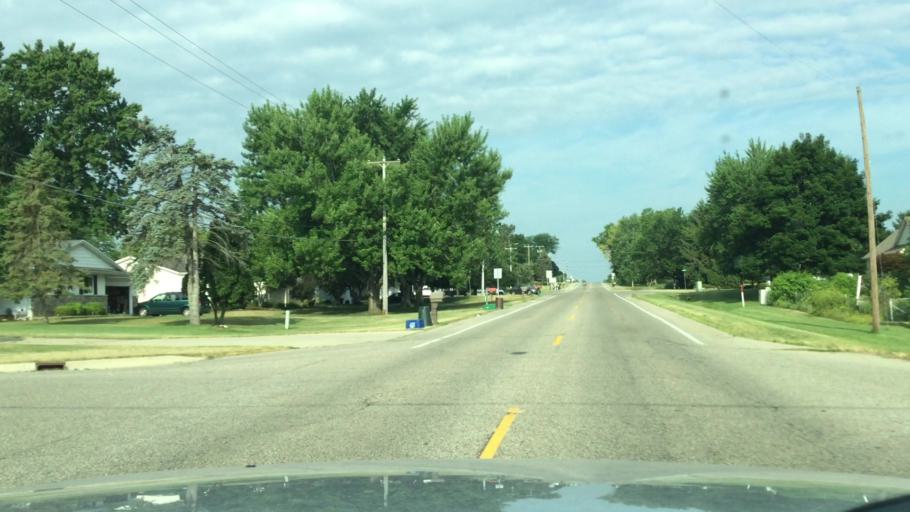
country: US
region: Michigan
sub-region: Genesee County
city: Flushing
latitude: 43.0597
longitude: -83.8649
